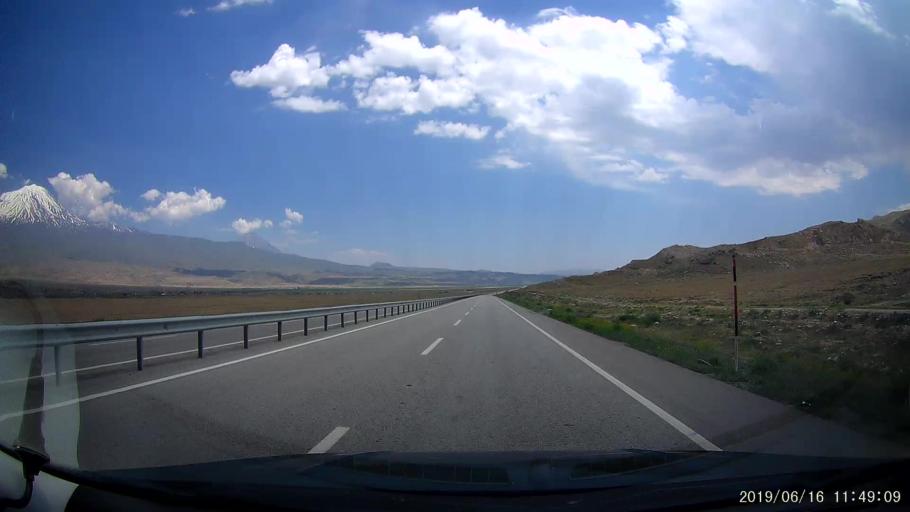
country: TR
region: Agri
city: Dogubayazit
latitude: 39.5576
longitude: 44.1580
